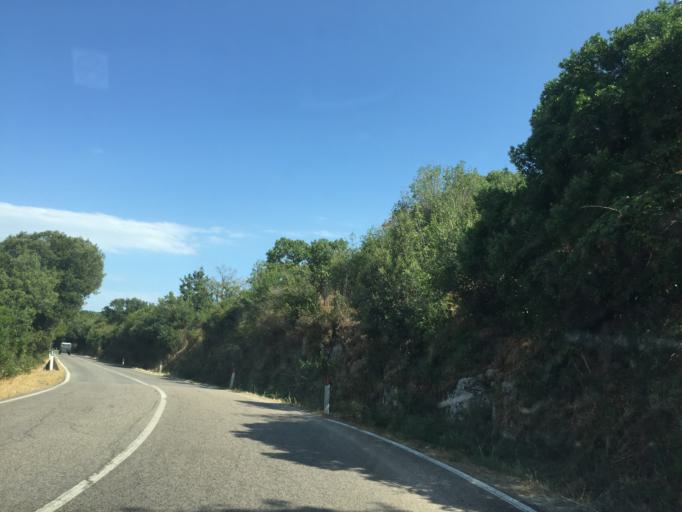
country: IT
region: Sardinia
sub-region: Provincia di Olbia-Tempio
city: Aggius
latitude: 40.9235
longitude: 9.0656
